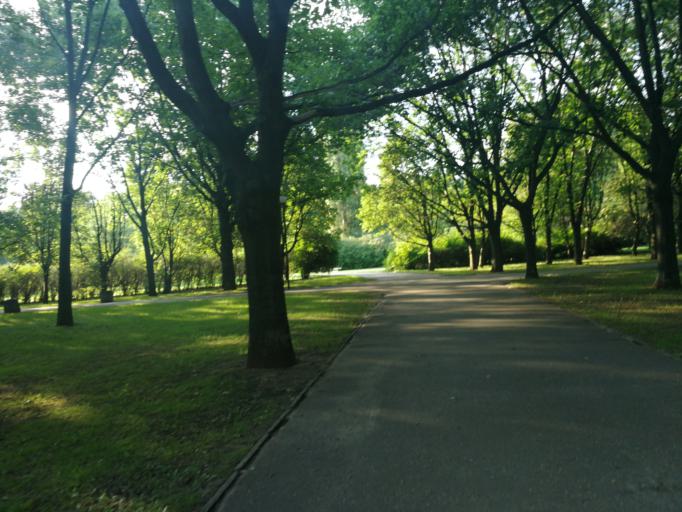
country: PL
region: Masovian Voivodeship
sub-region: Warszawa
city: Targowek
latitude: 52.2890
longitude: 21.0383
